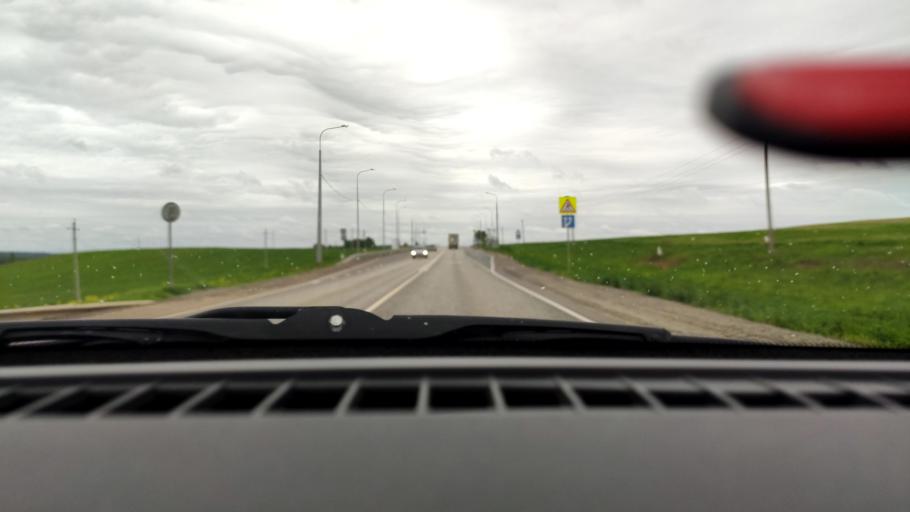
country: RU
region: Perm
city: Nytva
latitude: 58.0563
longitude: 55.1809
